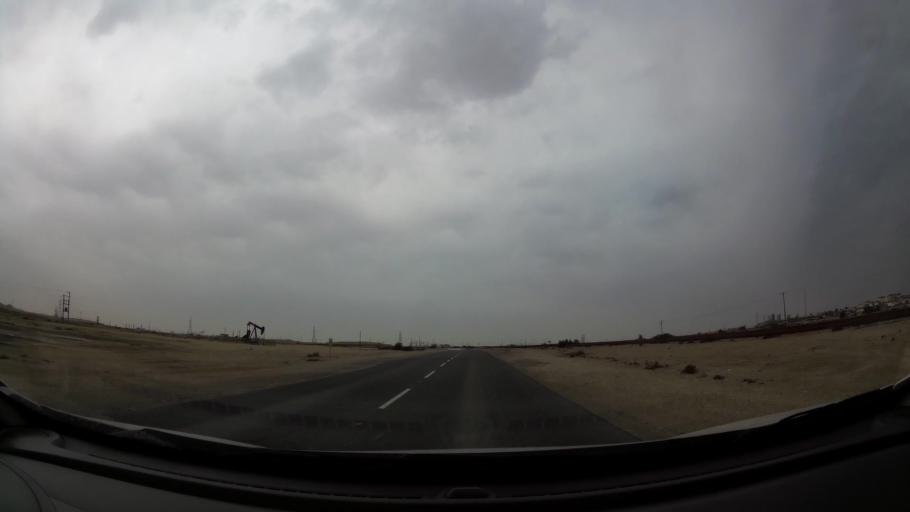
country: BH
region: Northern
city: Ar Rifa'
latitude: 26.0806
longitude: 50.5618
